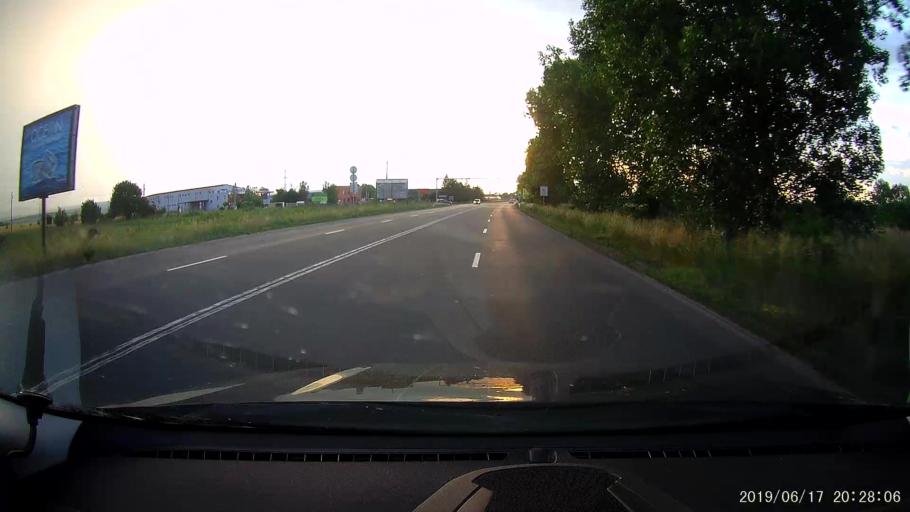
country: BG
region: Sofiya
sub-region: Obshtina Bozhurishte
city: Bozhurishte
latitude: 42.7757
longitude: 23.1823
